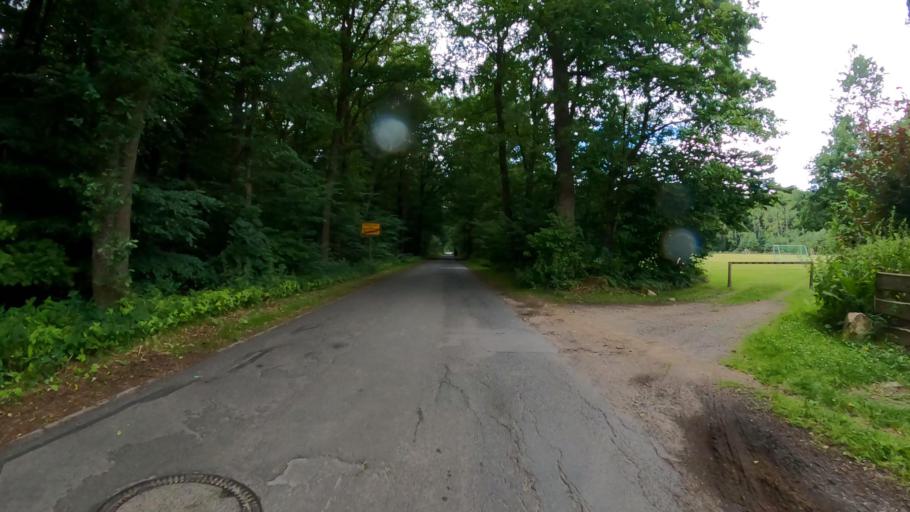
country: DE
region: Lower Saxony
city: Seevetal
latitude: 53.4173
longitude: 9.8858
